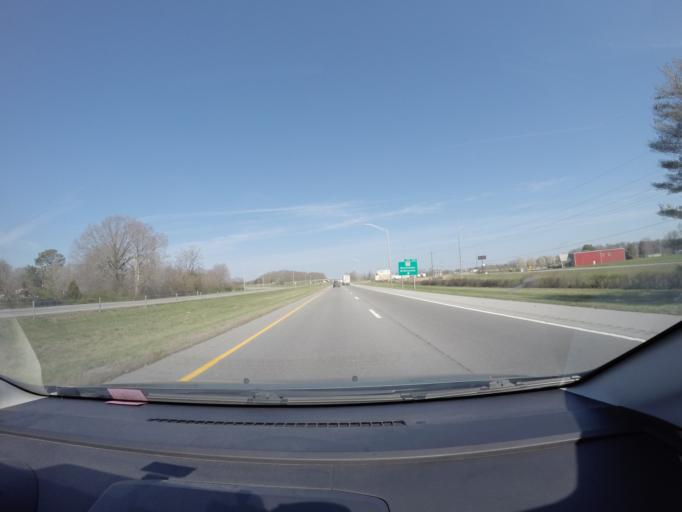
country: US
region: Tennessee
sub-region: Coffee County
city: Manchester
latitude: 35.4851
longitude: -86.0698
